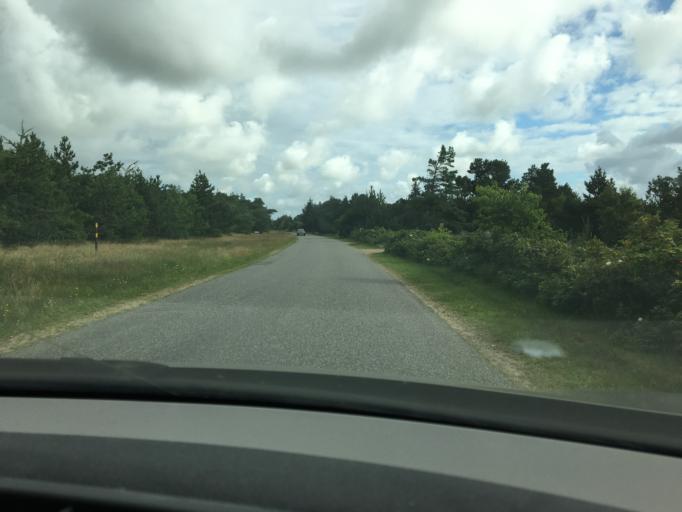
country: DK
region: Central Jutland
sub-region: Ringkobing-Skjern Kommune
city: Hvide Sande
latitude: 55.8208
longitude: 8.2154
